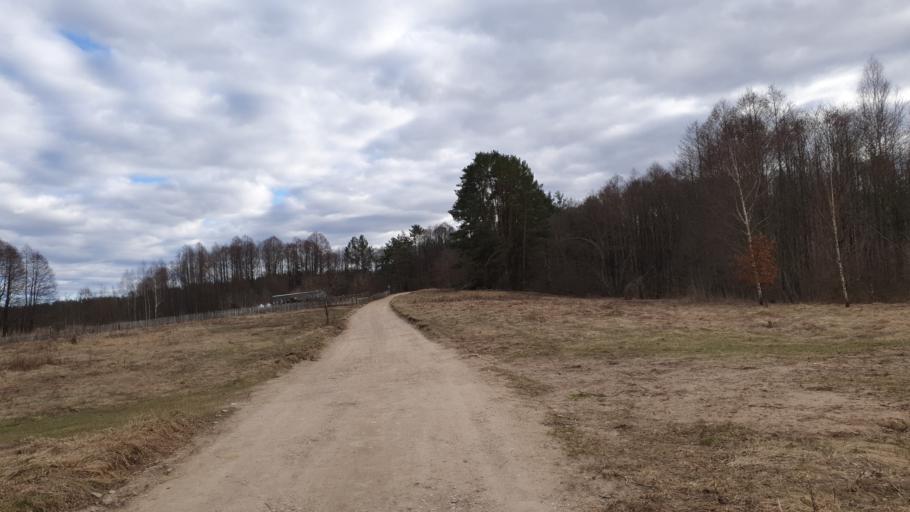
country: LT
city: Grigiskes
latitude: 54.7344
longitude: 25.0269
